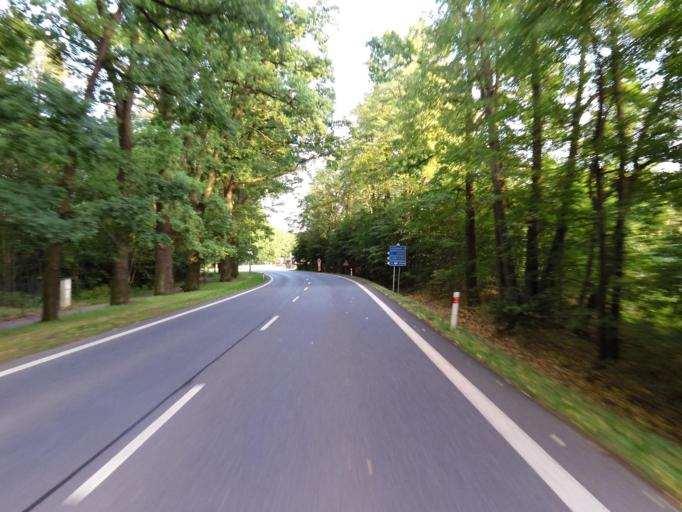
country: CZ
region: Jihocesky
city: Chlum u Trebone
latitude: 48.9497
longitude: 14.8697
